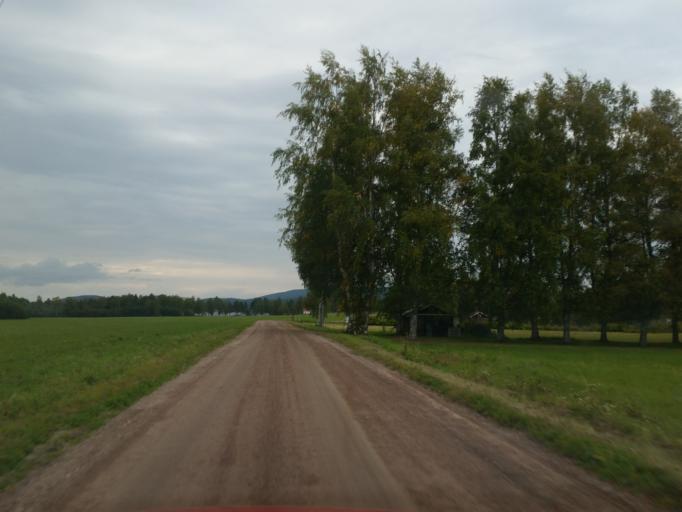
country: SE
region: Dalarna
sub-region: Leksand Municipality
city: Smedby
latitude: 60.6752
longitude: 15.1413
